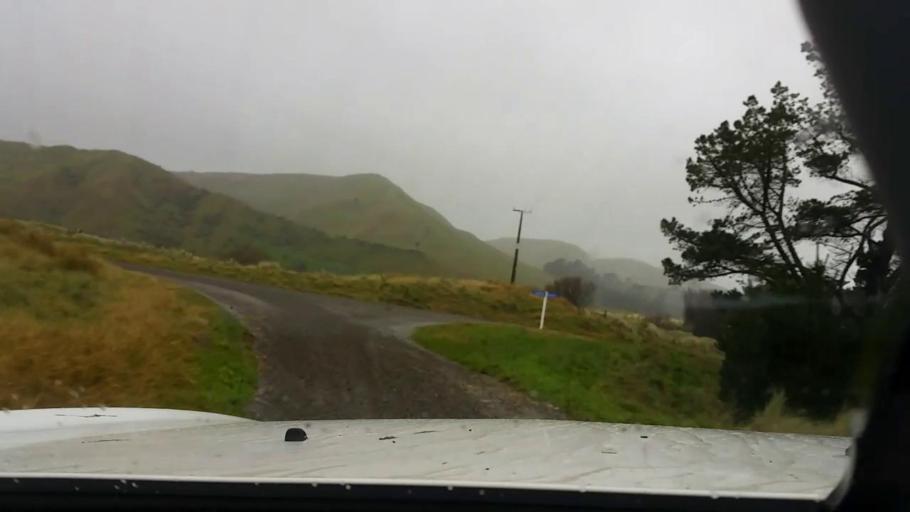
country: NZ
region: Wellington
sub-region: Masterton District
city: Masterton
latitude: -41.2523
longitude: 175.9154
